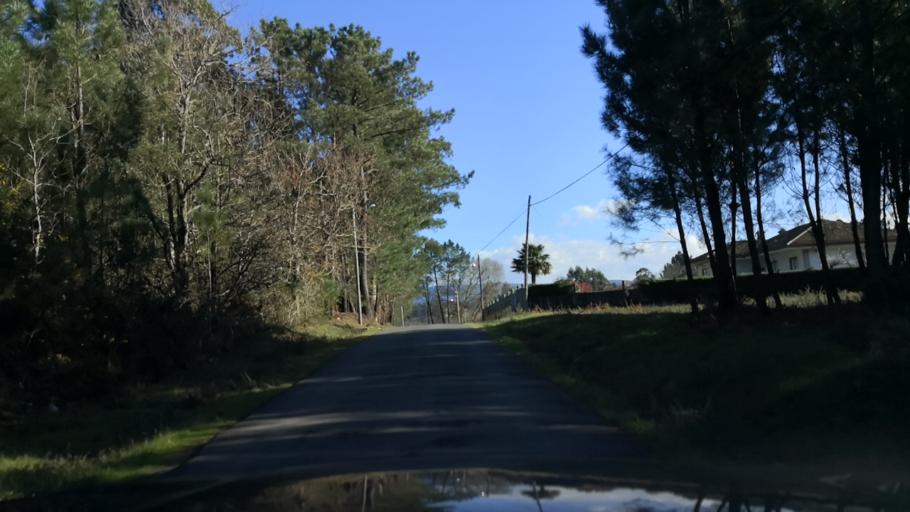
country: ES
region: Galicia
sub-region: Provincia da Coruna
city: Ribeira
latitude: 42.7174
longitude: -8.4409
